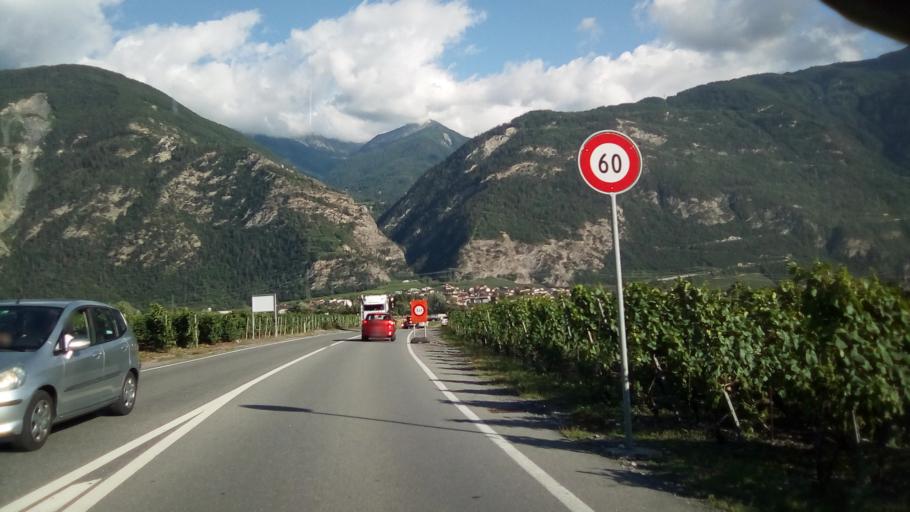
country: CH
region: Valais
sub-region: Martigny District
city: Leytron
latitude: 46.1836
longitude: 7.2143
